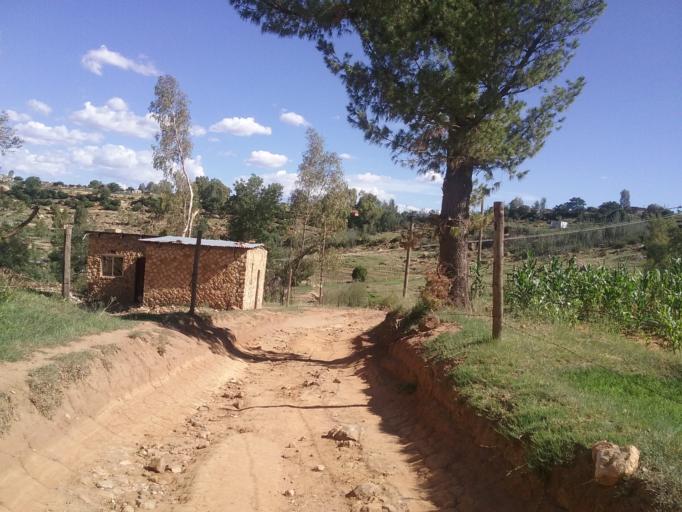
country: LS
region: Maseru
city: Maseru
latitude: -29.4185
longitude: 27.5695
